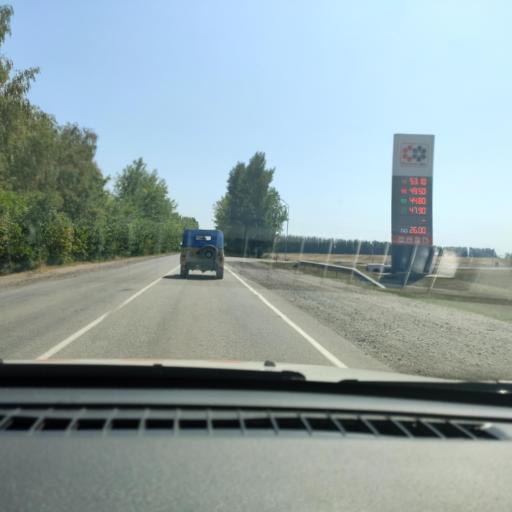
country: RU
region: Voronezj
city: Imeni Pervogo Maya
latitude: 50.7265
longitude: 39.4014
